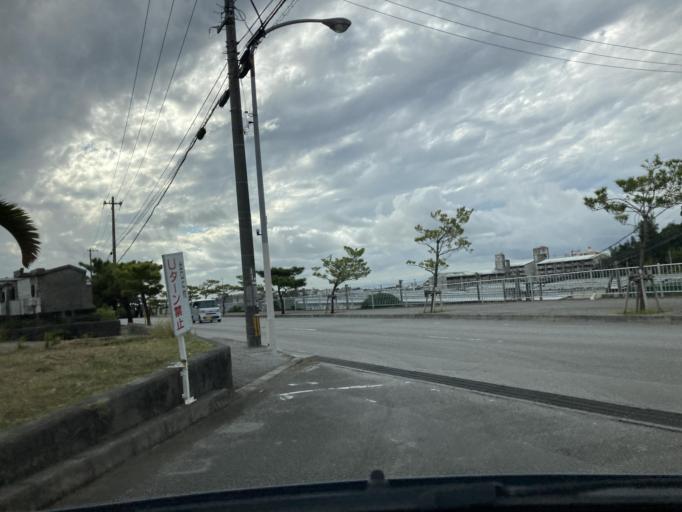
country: JP
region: Okinawa
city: Naha-shi
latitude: 26.2163
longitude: 127.7330
